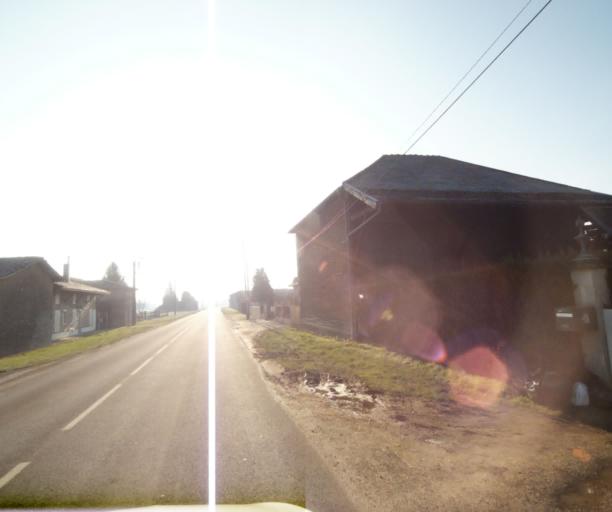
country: FR
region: Champagne-Ardenne
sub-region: Departement de la Haute-Marne
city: Montier-en-Der
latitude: 48.4597
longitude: 4.7682
